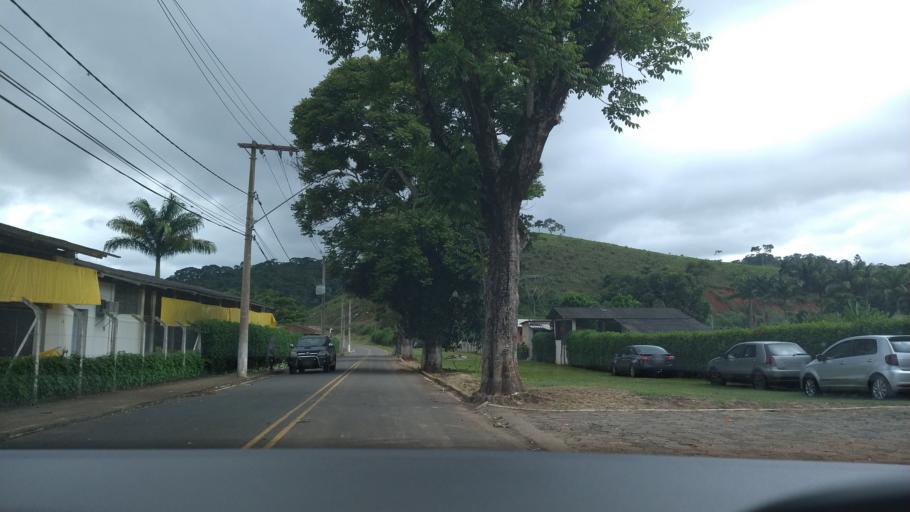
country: BR
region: Minas Gerais
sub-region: Vicosa
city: Vicosa
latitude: -20.7718
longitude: -42.8614
